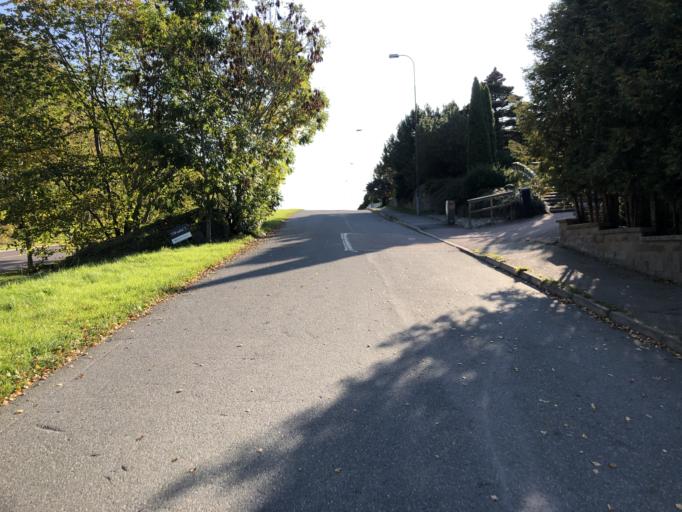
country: SE
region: Vaestra Goetaland
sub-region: Goteborg
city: Billdal
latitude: 57.6226
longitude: 11.9013
